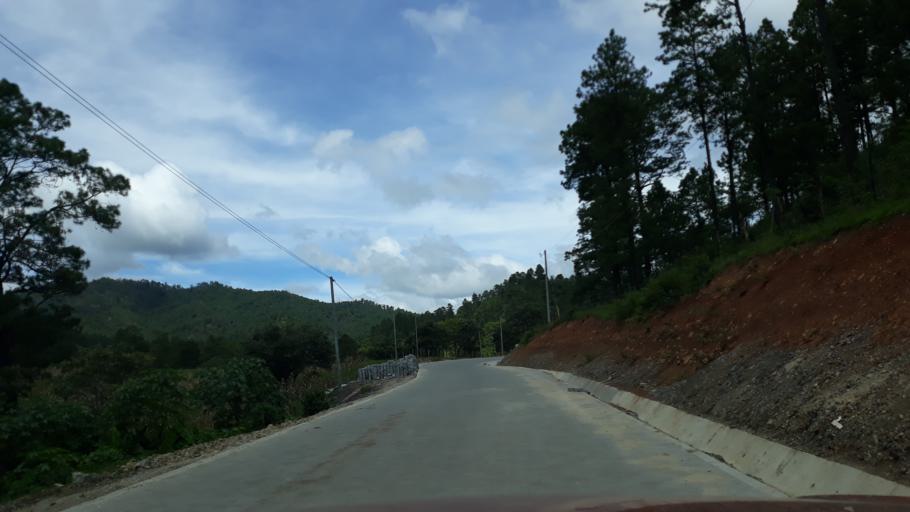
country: HN
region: El Paraiso
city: Santa Cruz
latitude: 13.7379
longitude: -86.6257
